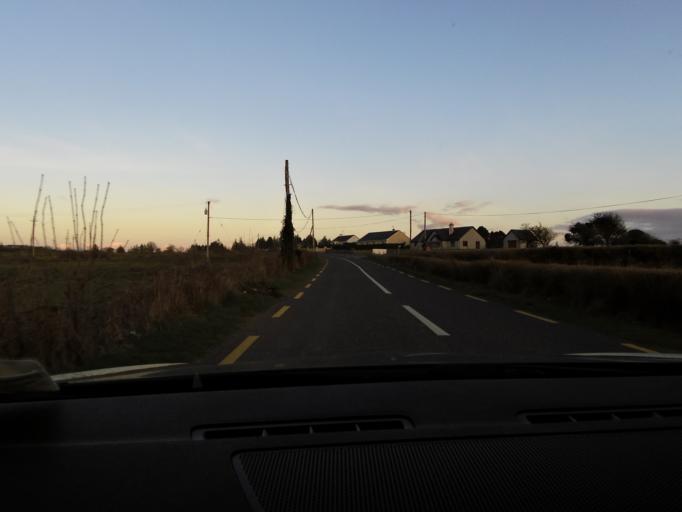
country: IE
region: Connaught
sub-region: Roscommon
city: Boyle
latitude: 53.9719
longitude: -8.4069
